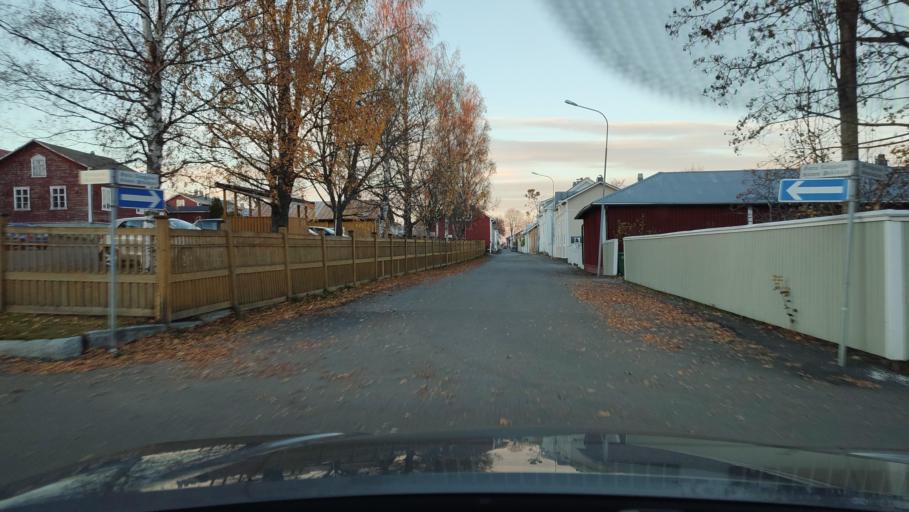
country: FI
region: Ostrobothnia
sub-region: Sydosterbotten
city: Kristinestad
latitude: 62.2691
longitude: 21.3759
